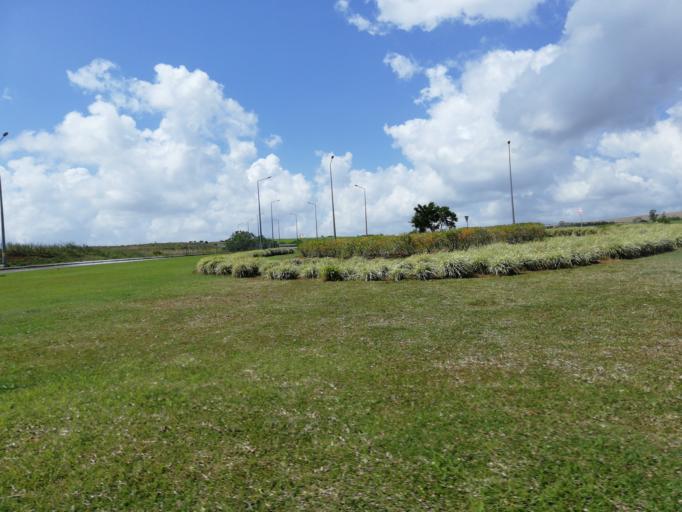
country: MU
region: Moka
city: Moka
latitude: -20.2338
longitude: 57.5091
